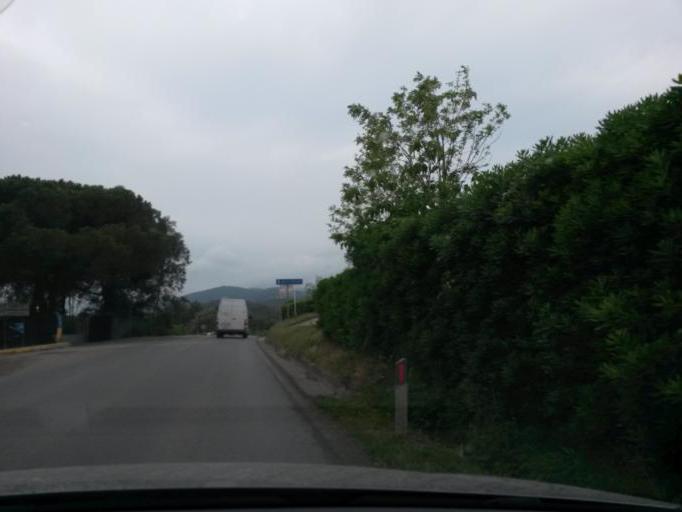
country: IT
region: Tuscany
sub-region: Provincia di Livorno
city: Capoliveri
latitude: 42.7620
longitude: 10.3632
